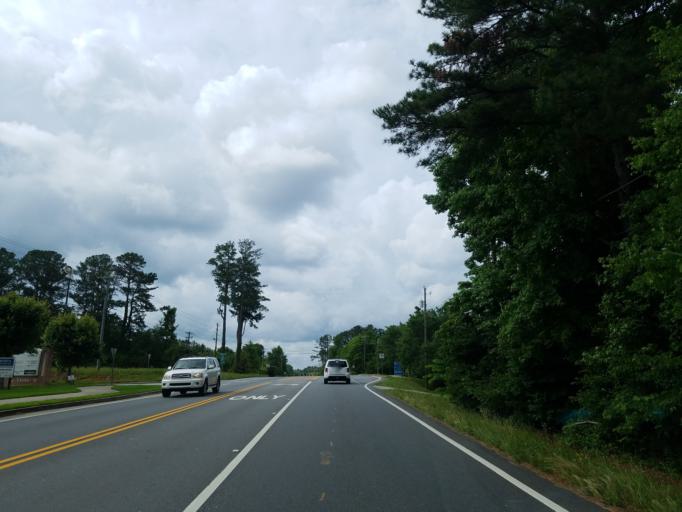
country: US
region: Georgia
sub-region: Fulton County
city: Milton
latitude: 34.1128
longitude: -84.2690
